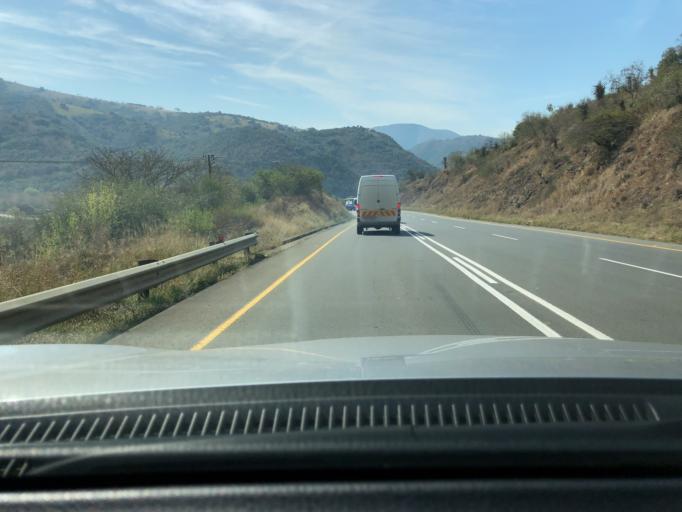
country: ZA
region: KwaZulu-Natal
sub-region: uMgungundlovu District Municipality
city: Richmond
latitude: -30.0127
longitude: 30.2410
